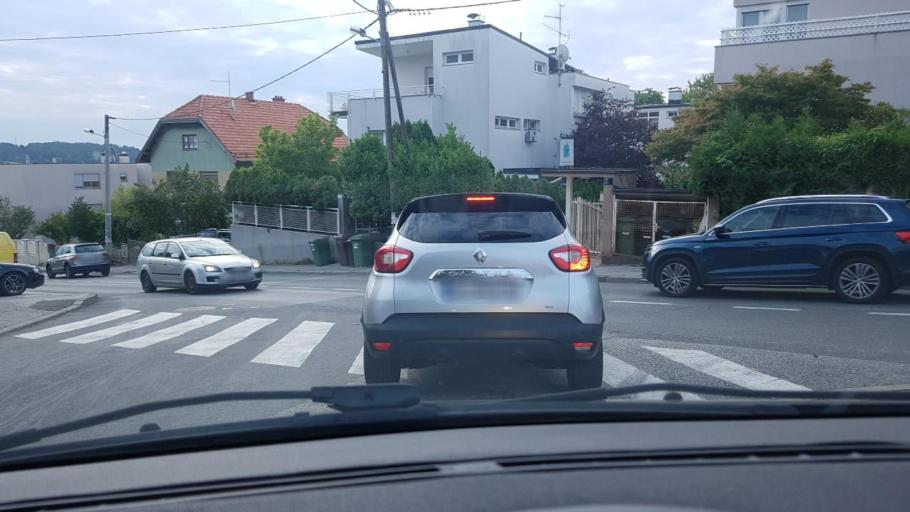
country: HR
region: Grad Zagreb
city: Zagreb
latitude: 45.8542
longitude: 15.9516
